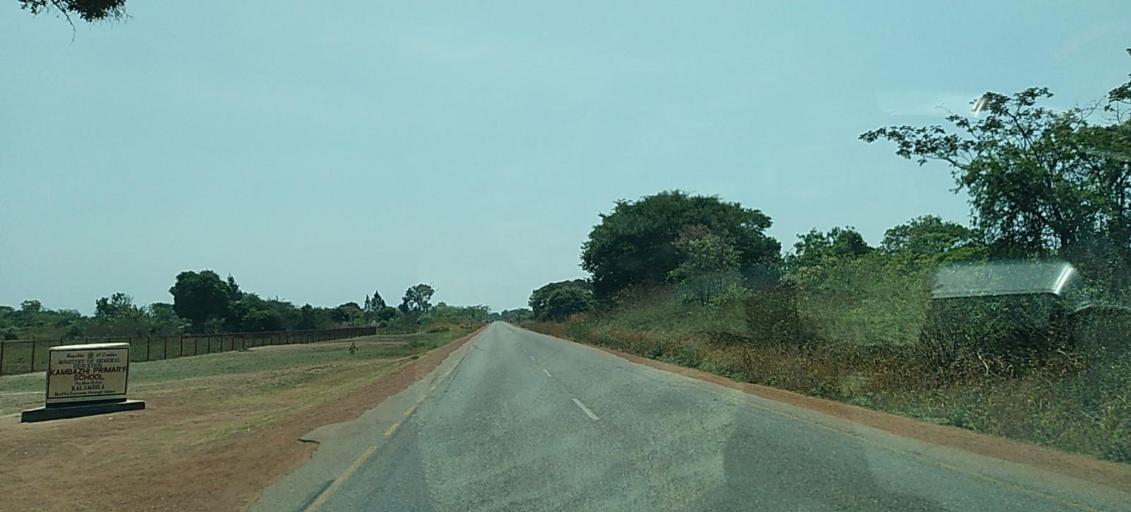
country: ZM
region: North-Western
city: Solwezi
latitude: -12.4058
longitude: 26.1372
